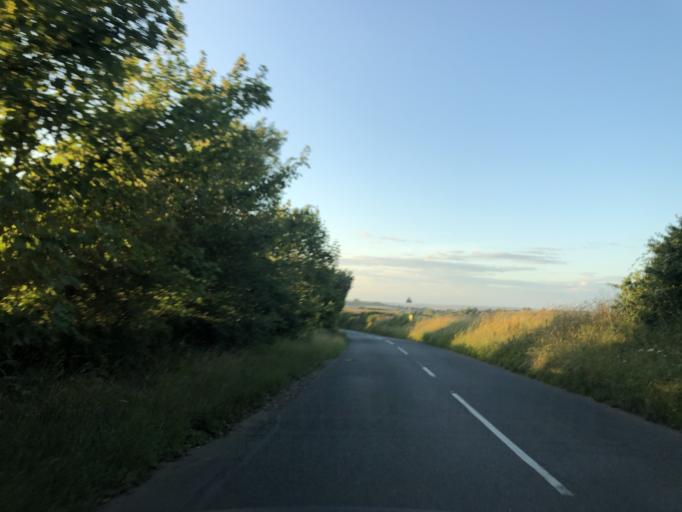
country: GB
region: England
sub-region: Isle of Wight
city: Niton
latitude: 50.6077
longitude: -1.2788
